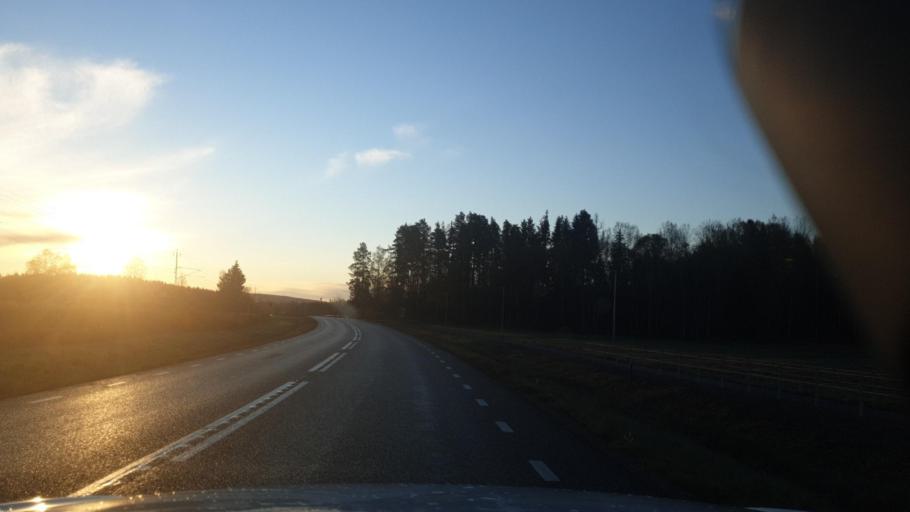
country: SE
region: Vaermland
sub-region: Arvika Kommun
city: Arvika
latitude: 59.6654
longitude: 12.5273
